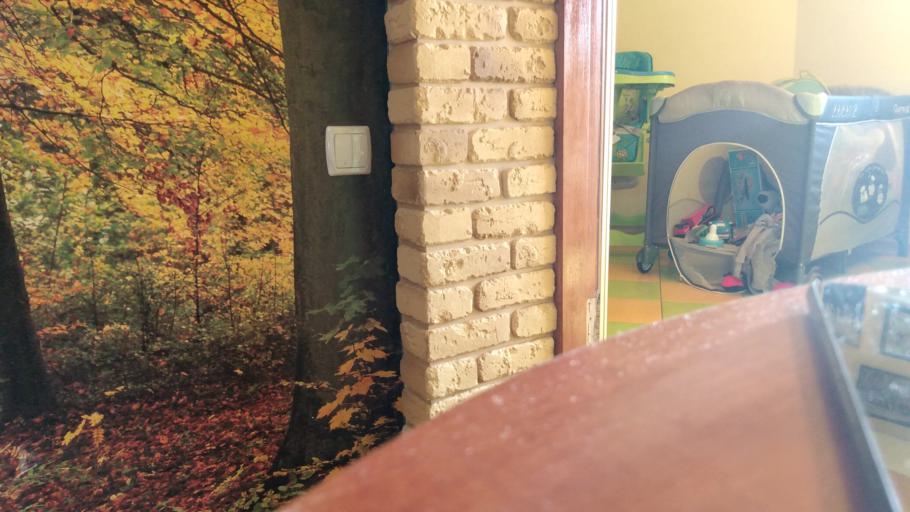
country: RU
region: Tverskaya
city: Vasil'yevskiy Mokh
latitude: 57.0440
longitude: 35.7999
